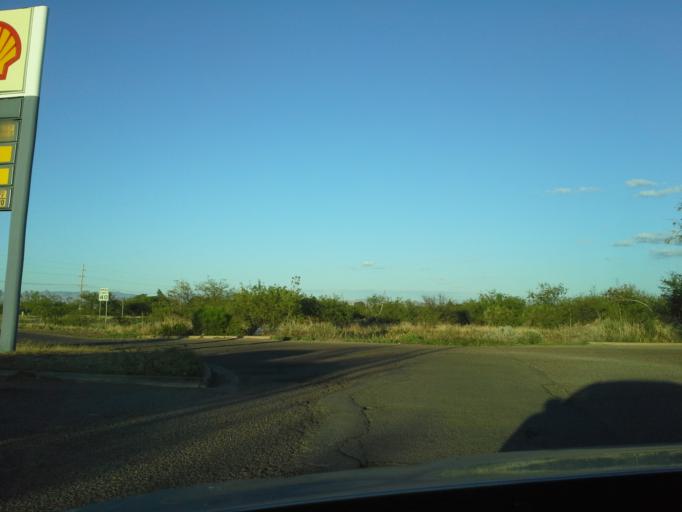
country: US
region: Arizona
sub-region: Cochise County
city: Huachuca City
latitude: 31.6924
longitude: -110.3493
